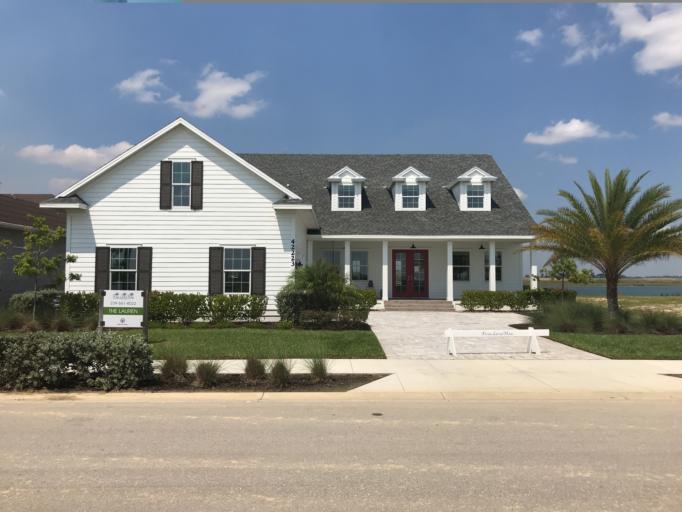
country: US
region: Florida
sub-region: Lee County
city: Fort Myers Shores
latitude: 26.7866
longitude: -81.7526
